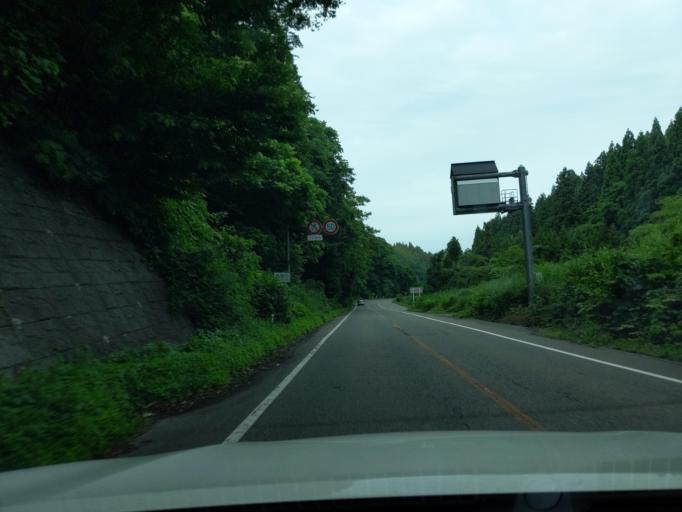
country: JP
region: Niigata
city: Nagaoka
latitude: 37.4440
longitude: 138.6998
